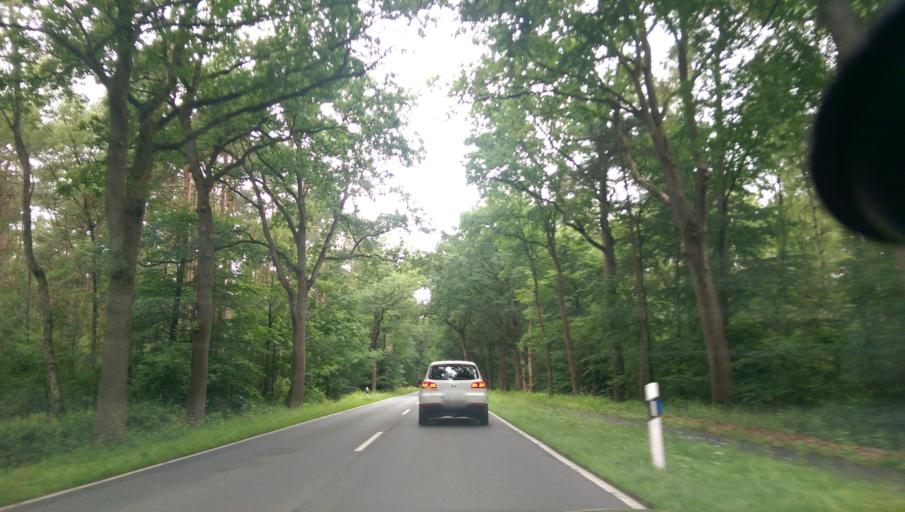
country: DE
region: Lower Saxony
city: Rotenburg
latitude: 53.0805
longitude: 9.4269
